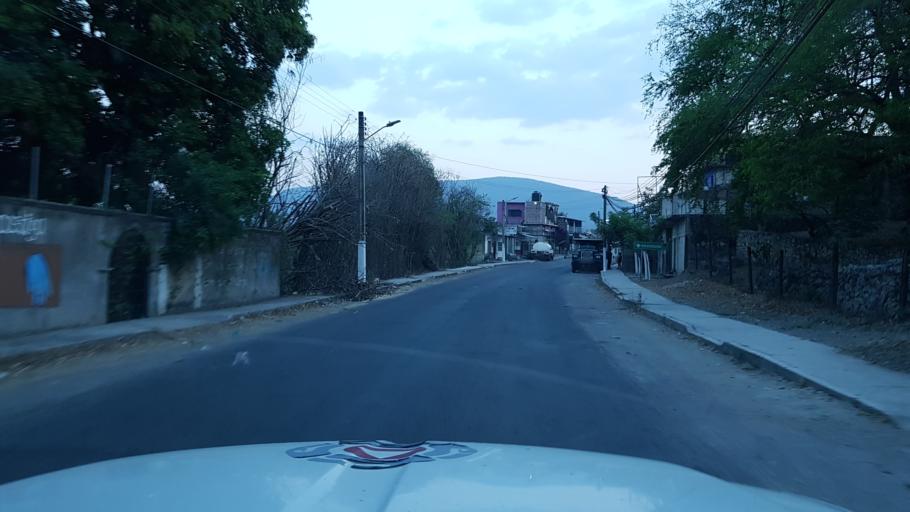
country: MX
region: Morelos
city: Tlaltizapan
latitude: 18.6936
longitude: -99.1136
